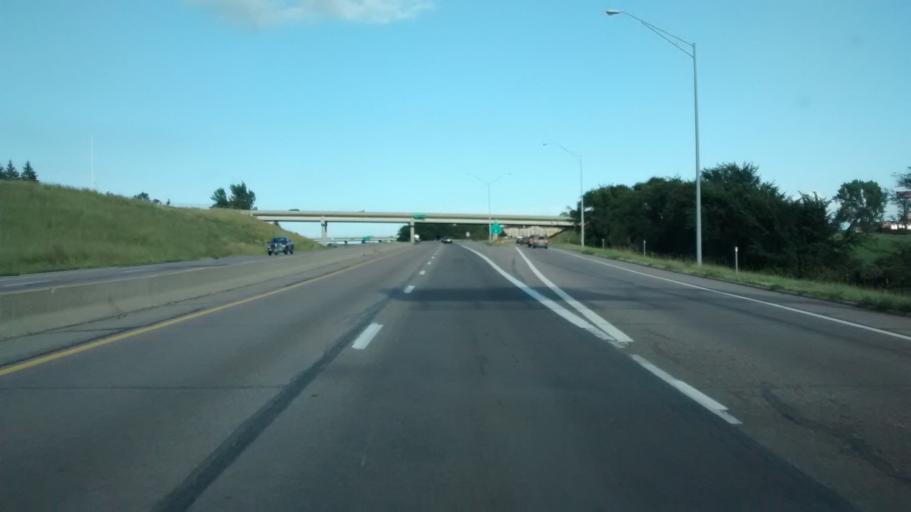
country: US
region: Iowa
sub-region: Woodbury County
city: Sergeant Bluff
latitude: 42.4440
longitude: -96.3559
